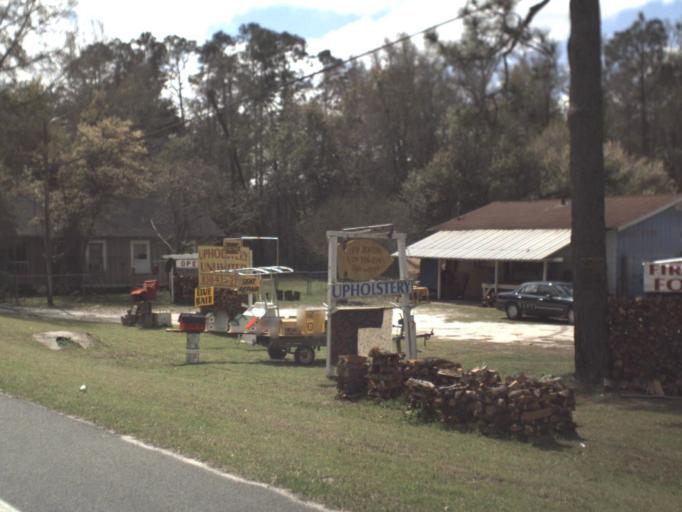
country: US
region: Florida
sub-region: Wakulla County
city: Crawfordville
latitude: 30.2261
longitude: -84.3624
